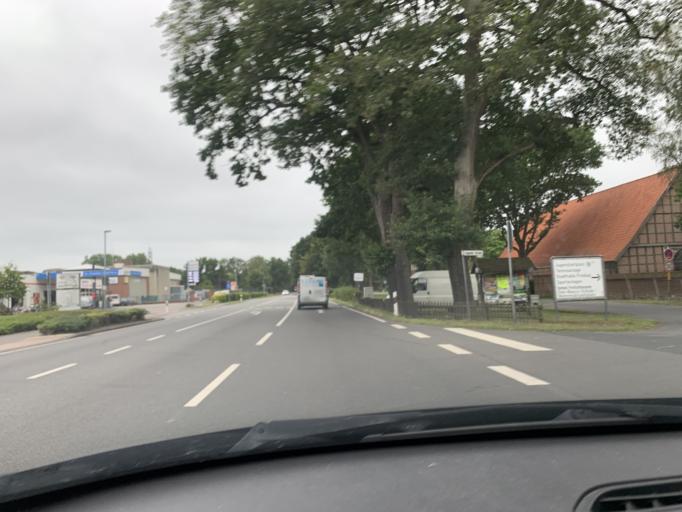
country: DE
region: Lower Saxony
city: Haselunne
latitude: 52.6684
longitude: 7.4846
